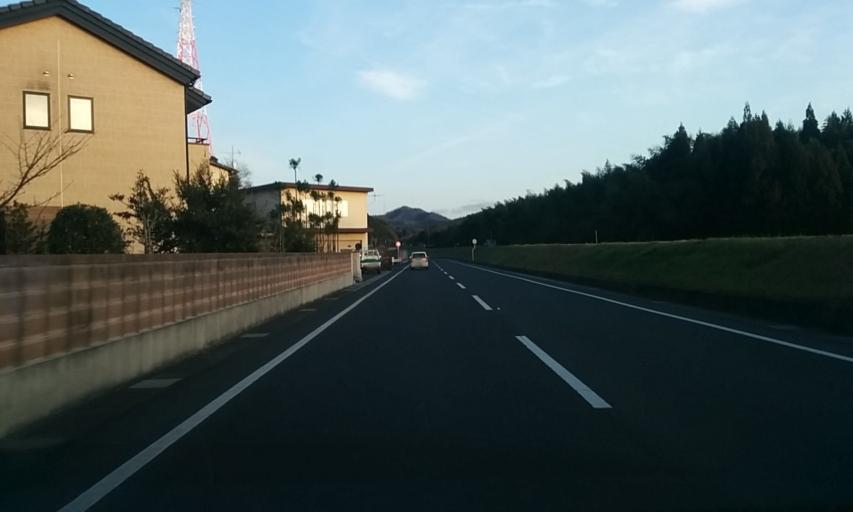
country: JP
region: Kyoto
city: Ayabe
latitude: 35.3125
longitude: 135.2547
